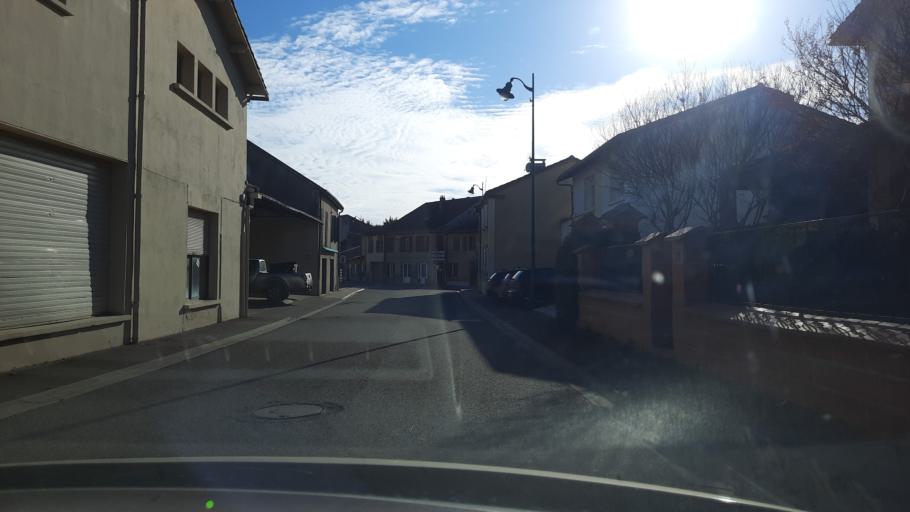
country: FR
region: Midi-Pyrenees
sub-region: Departement du Tarn-et-Garonne
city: Molieres
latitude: 44.1224
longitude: 1.3487
